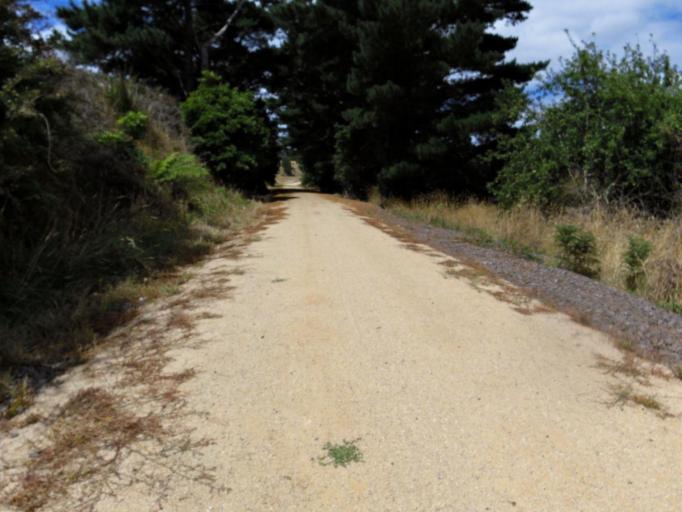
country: AU
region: Victoria
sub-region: Bass Coast
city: North Wonthaggi
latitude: -38.4175
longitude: 145.7846
